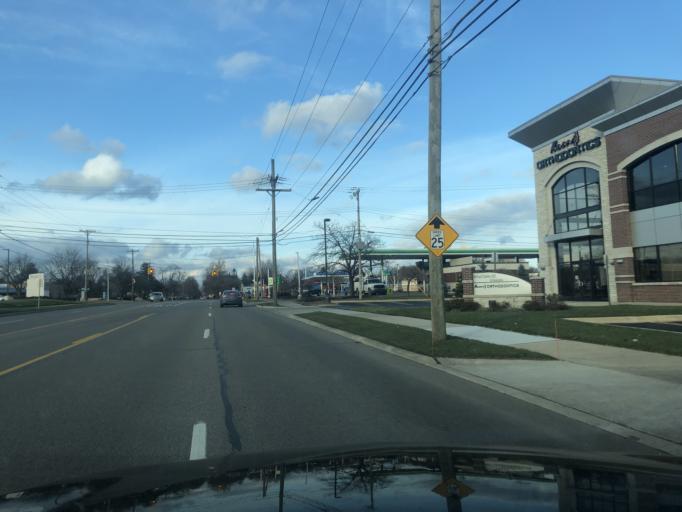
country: US
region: Michigan
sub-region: Wayne County
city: Livonia
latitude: 42.3956
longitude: -83.4028
